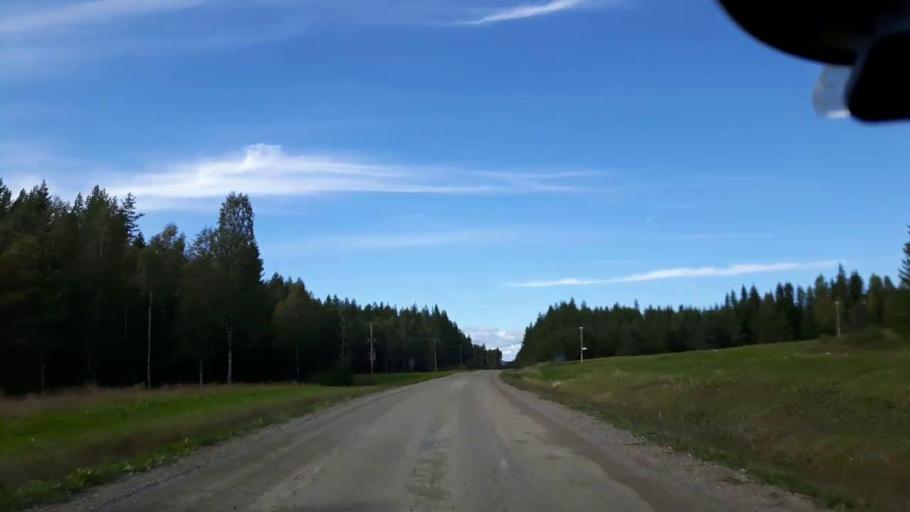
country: SE
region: Jaemtland
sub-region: Ragunda Kommun
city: Hammarstrand
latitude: 63.1377
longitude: 16.2398
